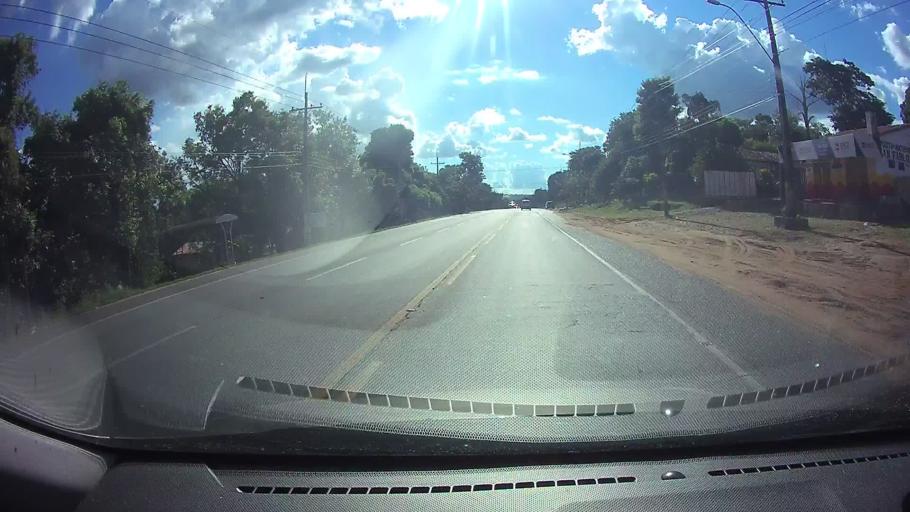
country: PY
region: Cordillera
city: Caacupe
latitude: -25.3882
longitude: -57.1090
